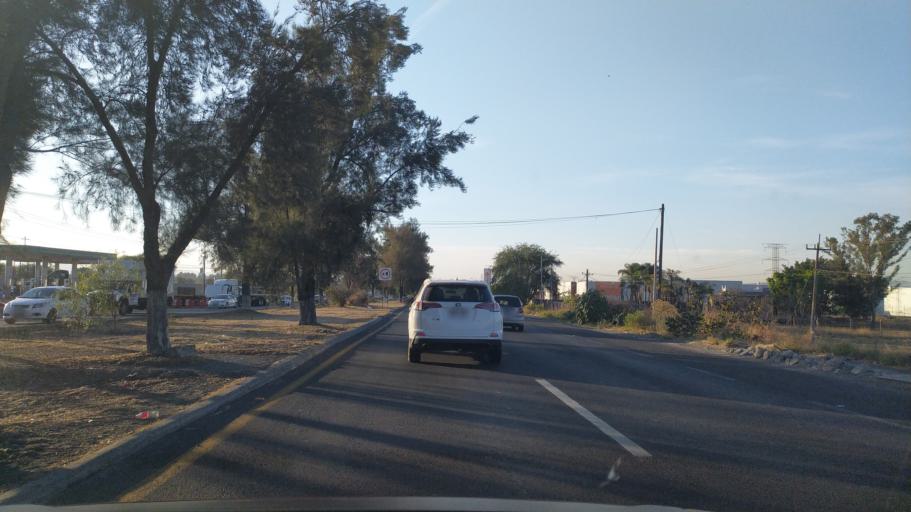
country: MX
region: Jalisco
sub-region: Tlajomulco de Zuniga
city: Rancho Alegre [Fraccionamiento]
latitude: 20.4768
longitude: -103.2646
